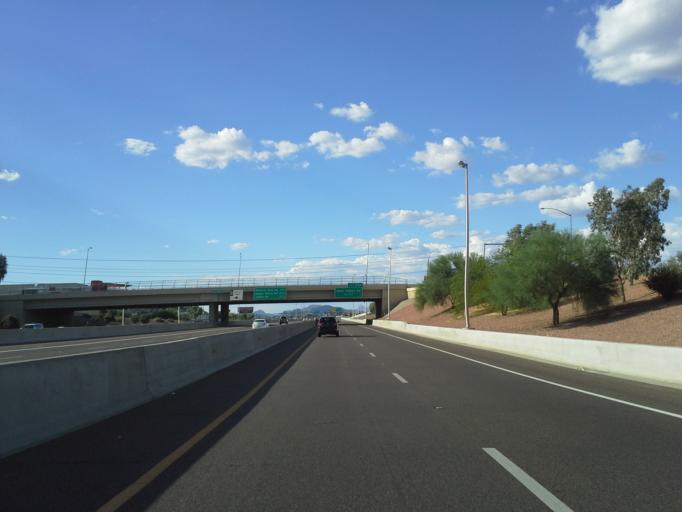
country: US
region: Arizona
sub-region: Maricopa County
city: Glendale
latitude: 33.6751
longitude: -112.1126
